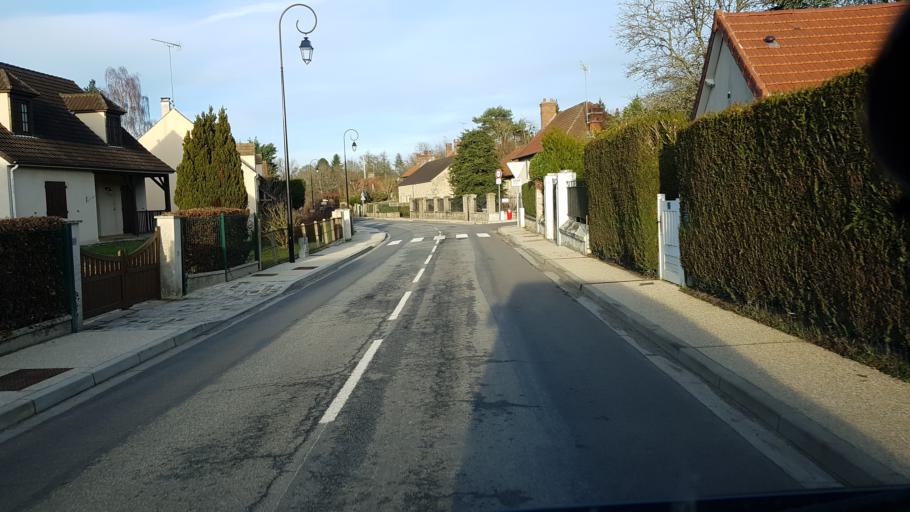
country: FR
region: Ile-de-France
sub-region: Departement des Yvelines
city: Gazeran
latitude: 48.6744
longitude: 1.7516
